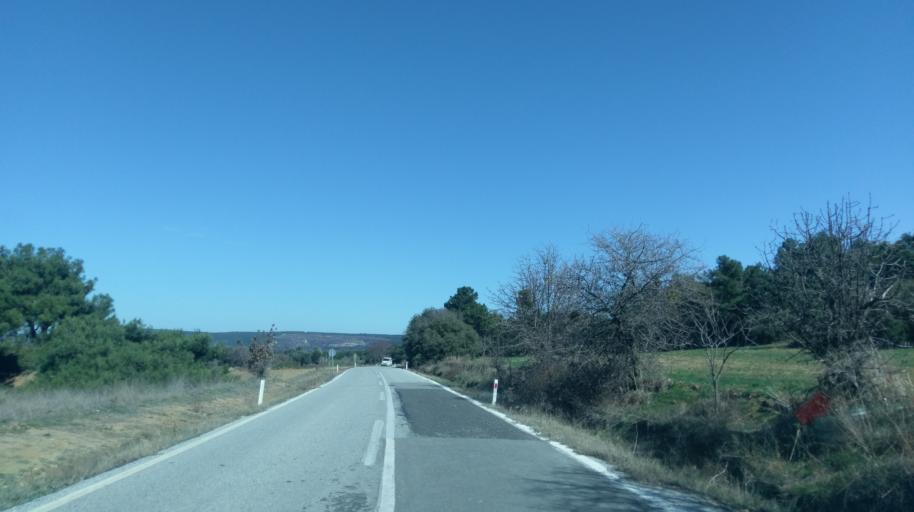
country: TR
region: Canakkale
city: Eceabat
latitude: 40.1126
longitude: 26.2519
